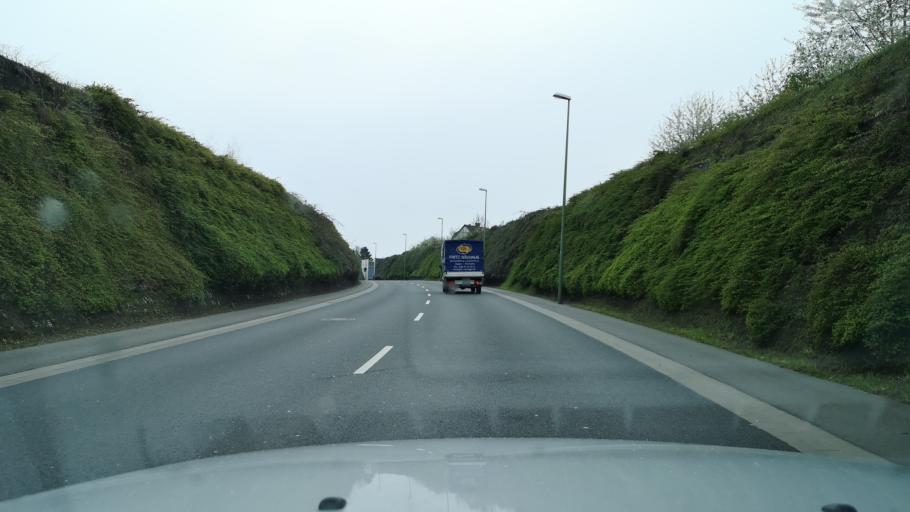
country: DE
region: North Rhine-Westphalia
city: Herdecke
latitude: 51.3954
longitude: 7.4657
